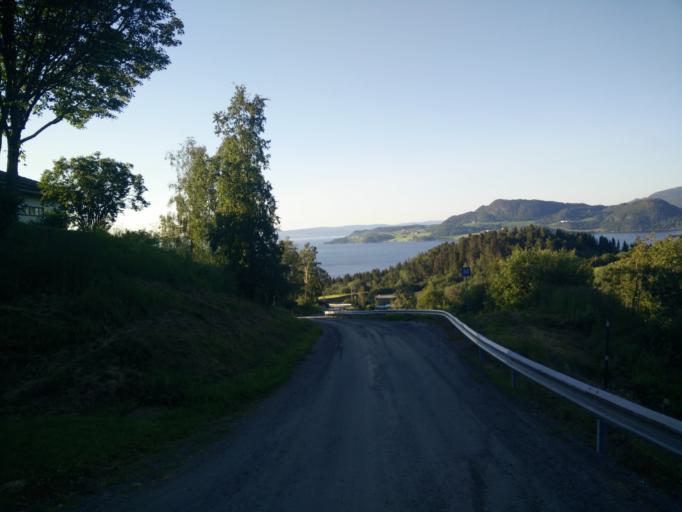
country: NO
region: Sor-Trondelag
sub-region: Skaun
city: Borsa
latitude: 63.3429
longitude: 10.0396
